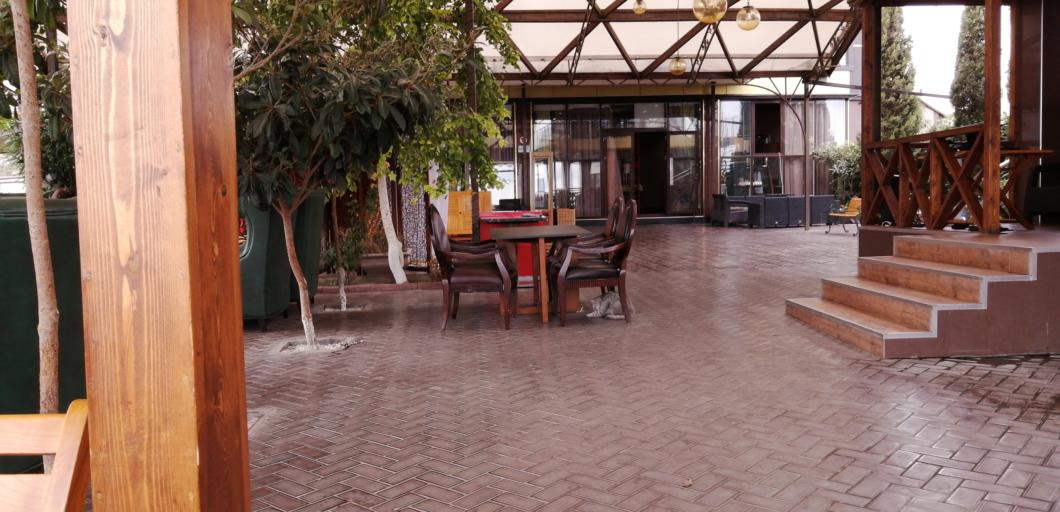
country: RU
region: Dagestan
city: Derbent
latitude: 42.0526
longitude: 48.3116
